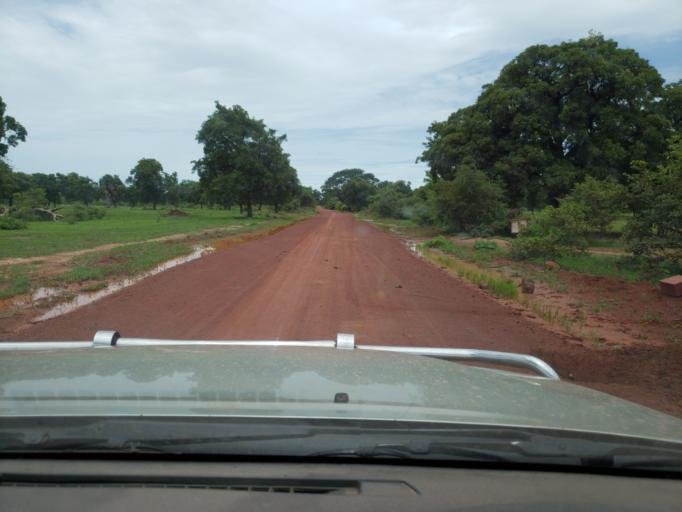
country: ML
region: Sikasso
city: Sikasso
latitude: 11.6678
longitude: -6.3421
